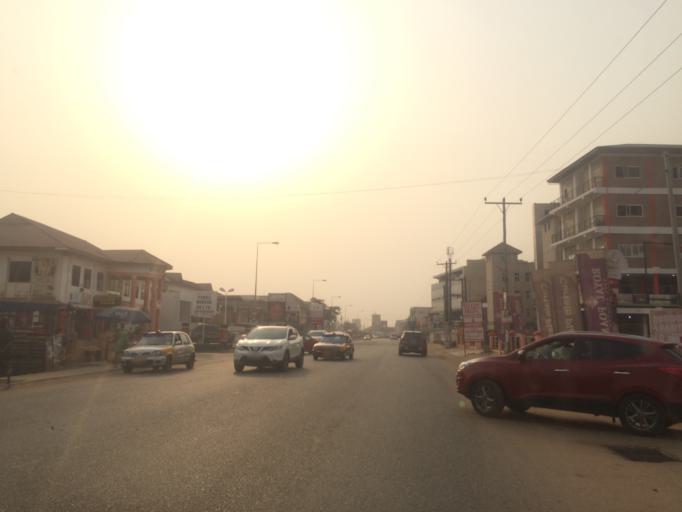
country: GH
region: Greater Accra
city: Nungua
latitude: 5.6235
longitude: -0.0734
